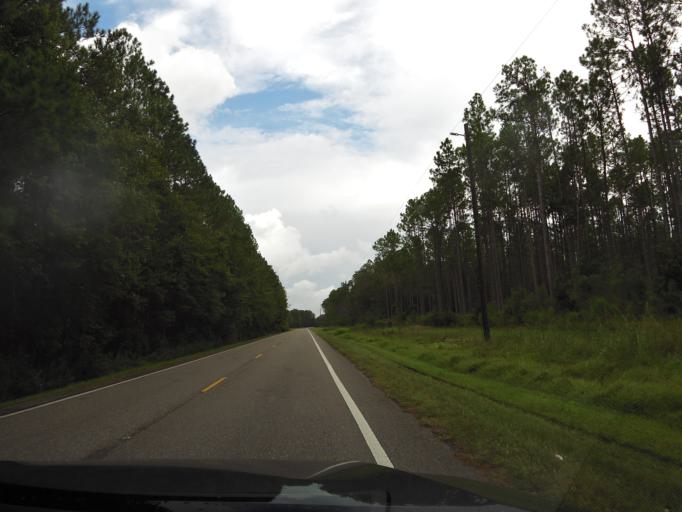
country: US
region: Florida
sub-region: Duval County
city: Baldwin
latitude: 30.3687
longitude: -81.9275
